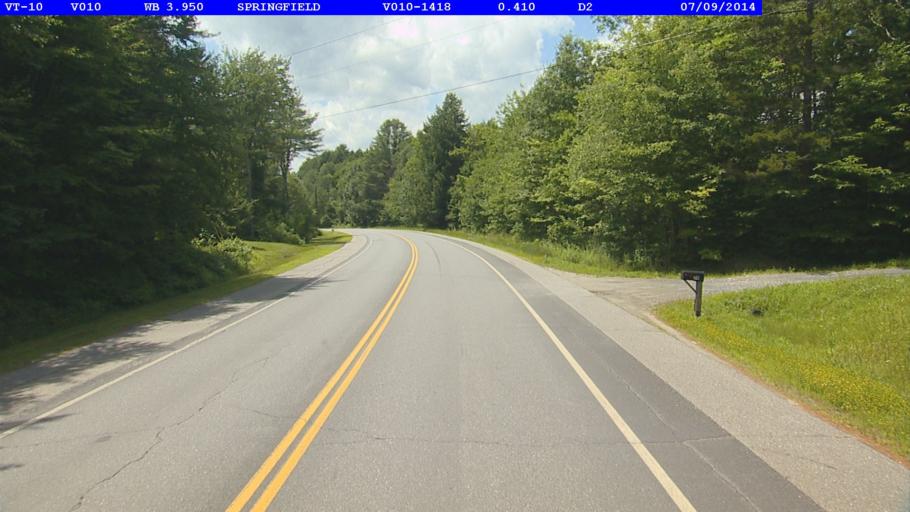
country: US
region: Vermont
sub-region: Windsor County
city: Springfield
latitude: 43.3368
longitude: -72.5390
